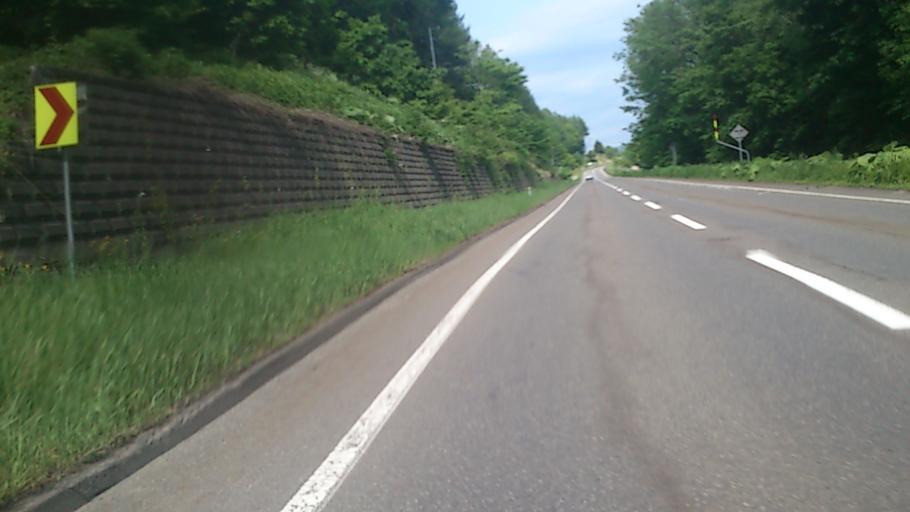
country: JP
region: Hokkaido
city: Otofuke
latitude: 43.2915
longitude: 143.6611
